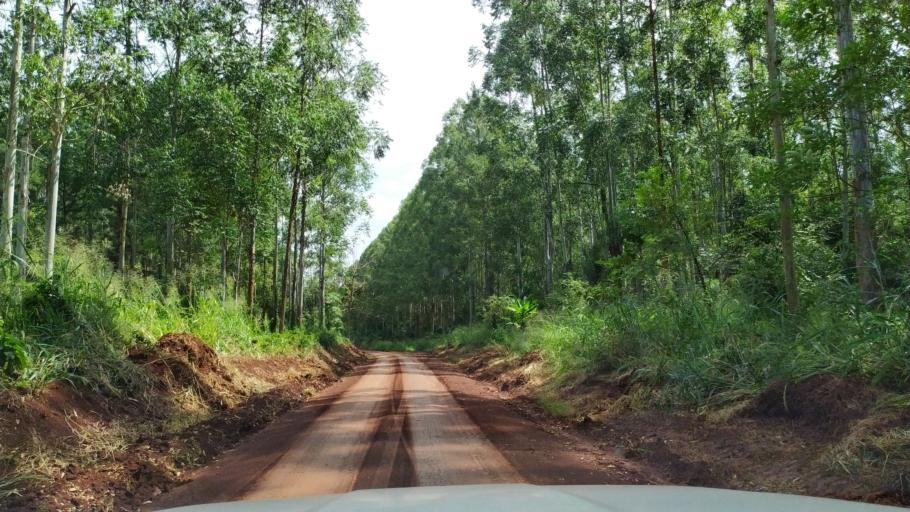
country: AR
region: Misiones
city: Puerto Piray
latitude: -26.5321
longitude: -54.6270
